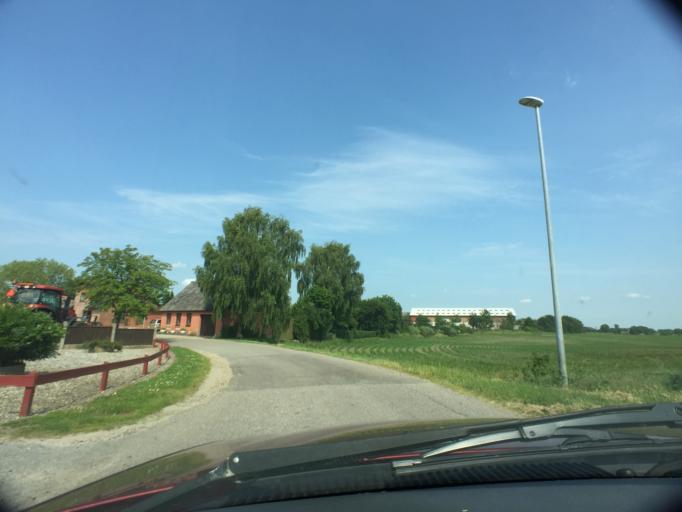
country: DK
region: Central Jutland
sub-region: Viborg Kommune
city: Bjerringbro
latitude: 56.2518
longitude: 9.7112
